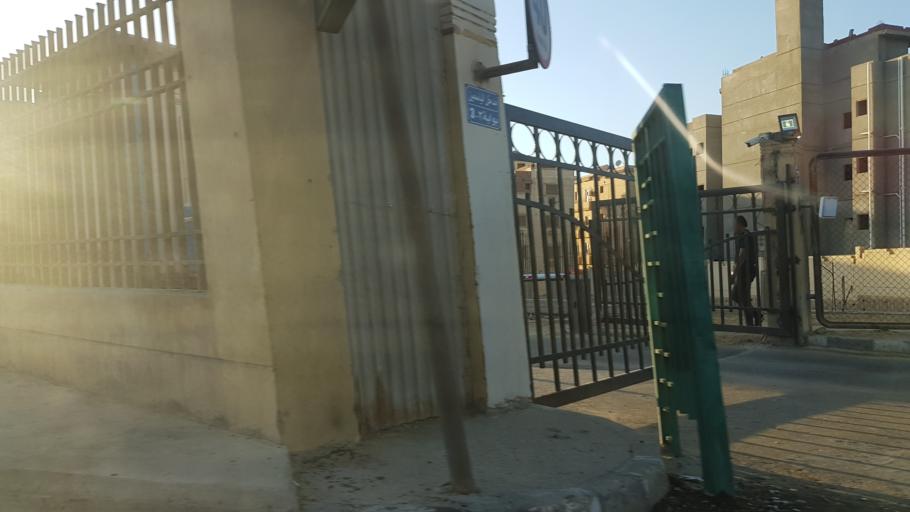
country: EG
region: Muhafazat al Qalyubiyah
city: Al Khankah
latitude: 30.0611
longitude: 31.4438
